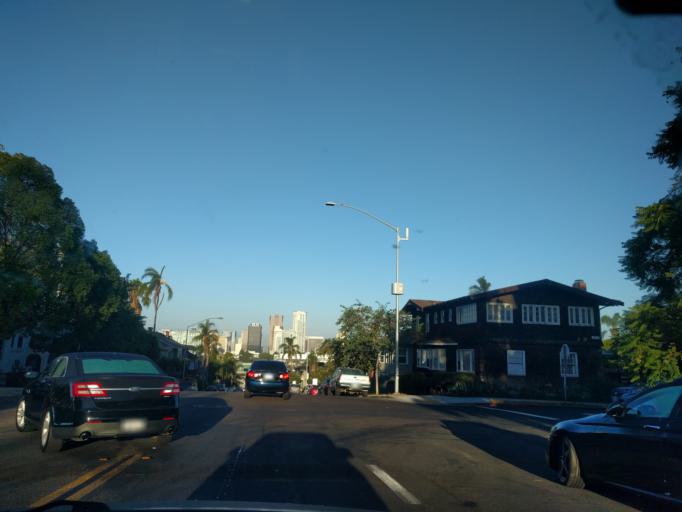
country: US
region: California
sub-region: San Diego County
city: San Diego
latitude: 32.7179
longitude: -117.1424
